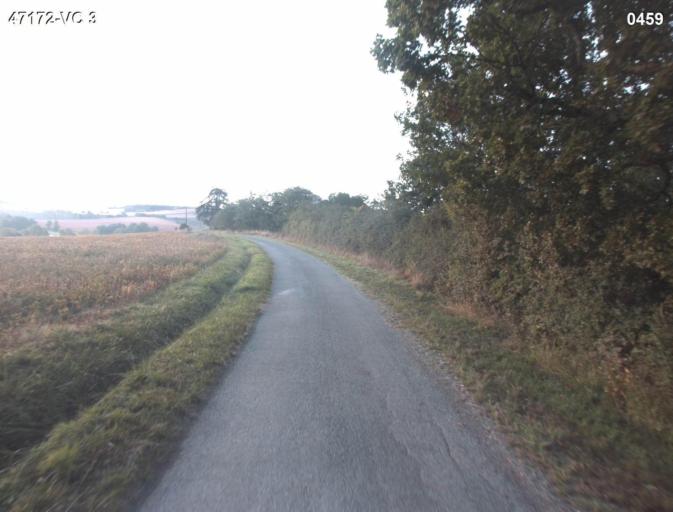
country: FR
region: Aquitaine
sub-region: Departement du Lot-et-Garonne
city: Sainte-Colombe-en-Bruilhois
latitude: 44.1658
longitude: 0.4929
